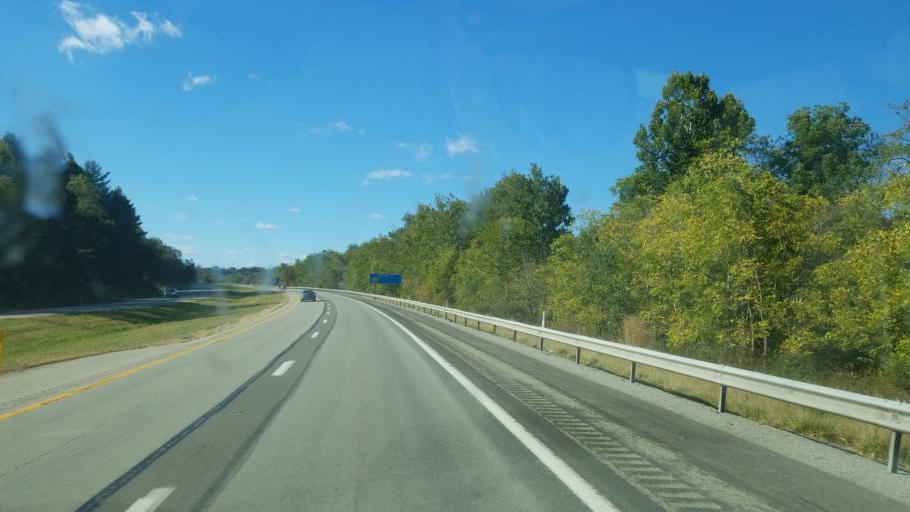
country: US
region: Pennsylvania
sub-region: Washington County
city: East Washington
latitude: 40.1008
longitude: -80.1952
